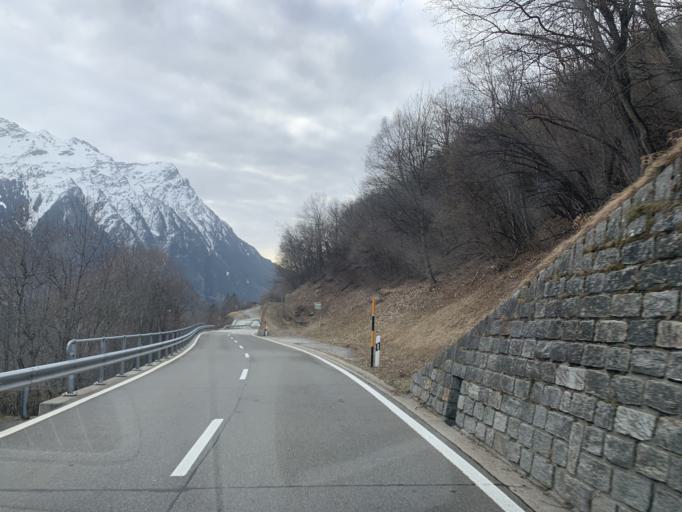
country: CH
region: Ticino
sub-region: Blenio District
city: Acquarossa
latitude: 46.5170
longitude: 8.9339
